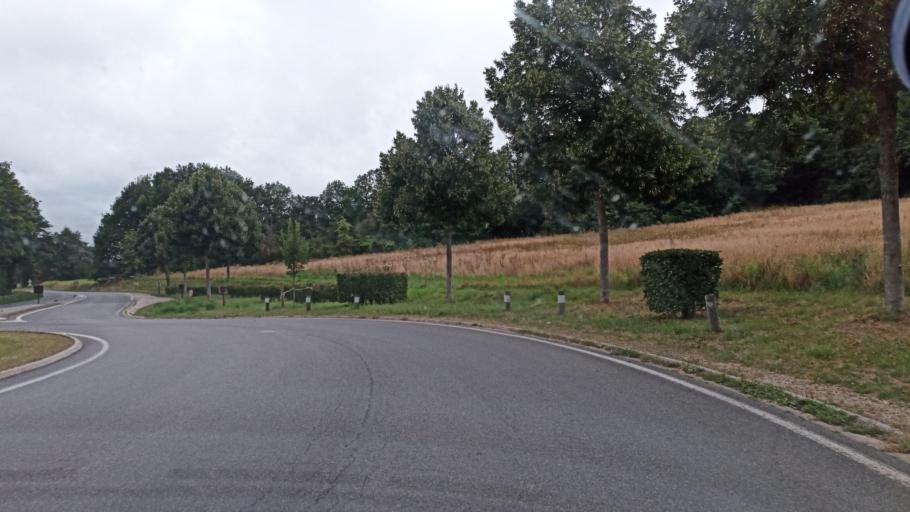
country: FR
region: Ile-de-France
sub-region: Departement de Seine-et-Marne
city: Voulx
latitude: 48.2893
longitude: 2.9566
